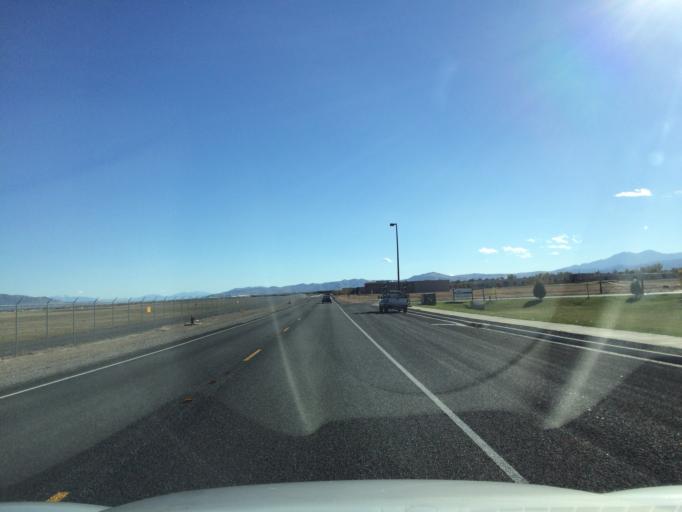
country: US
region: Utah
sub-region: Salt Lake County
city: Kearns
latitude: 40.6349
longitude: -111.9998
